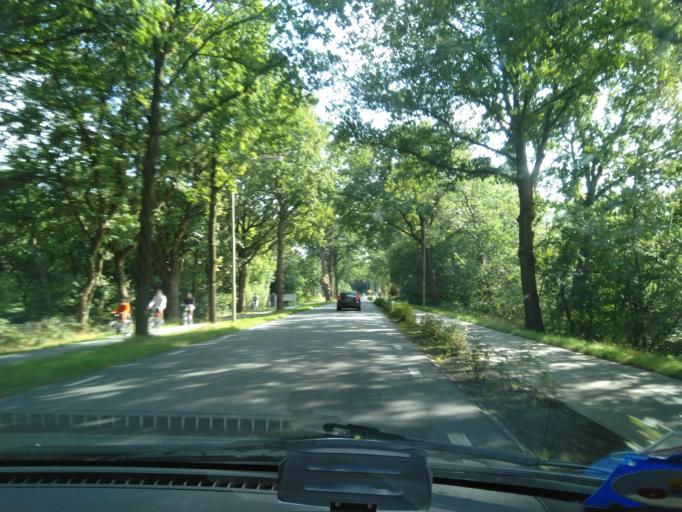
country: NL
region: Groningen
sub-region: Gemeente Groningen
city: Groningen
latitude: 53.1664
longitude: 6.5550
